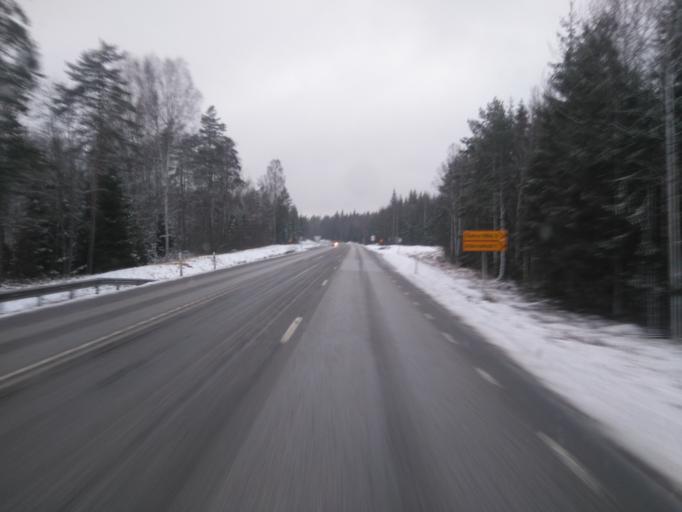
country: SE
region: Joenkoeping
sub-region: Eksjo Kommun
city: Eksjoe
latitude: 57.6470
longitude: 15.0573
